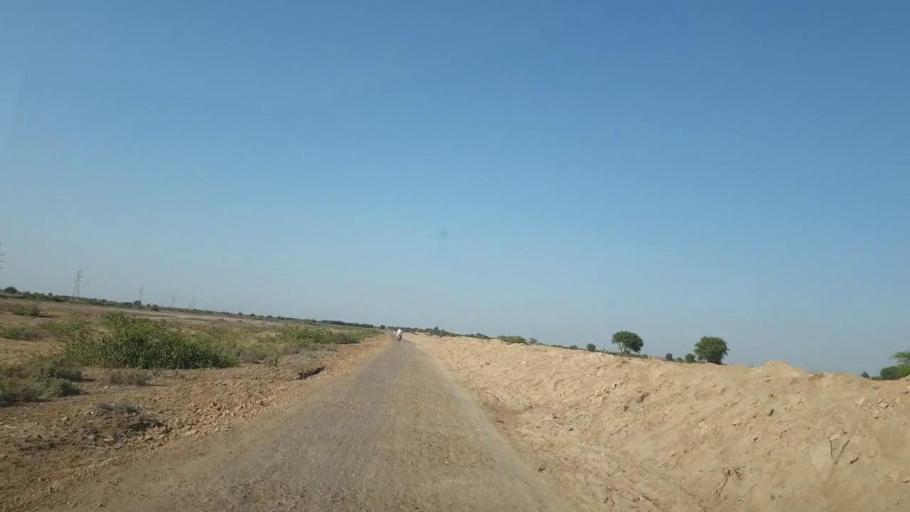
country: PK
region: Sindh
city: Naukot
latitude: 25.0379
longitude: 69.4421
